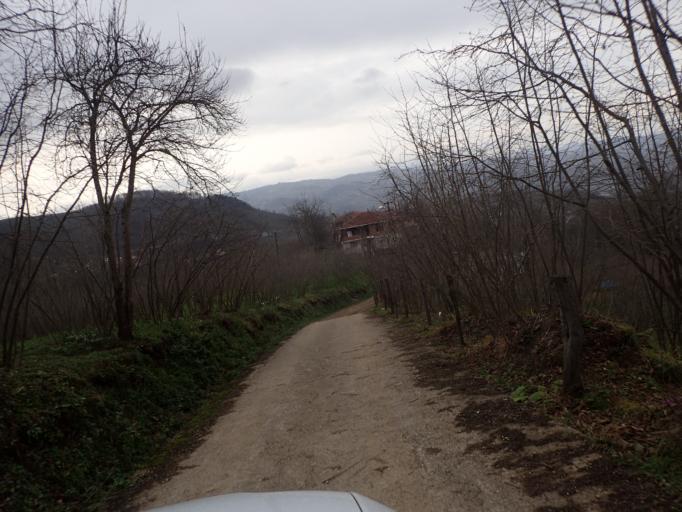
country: TR
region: Ordu
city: Camas
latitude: 40.9171
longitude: 37.5177
